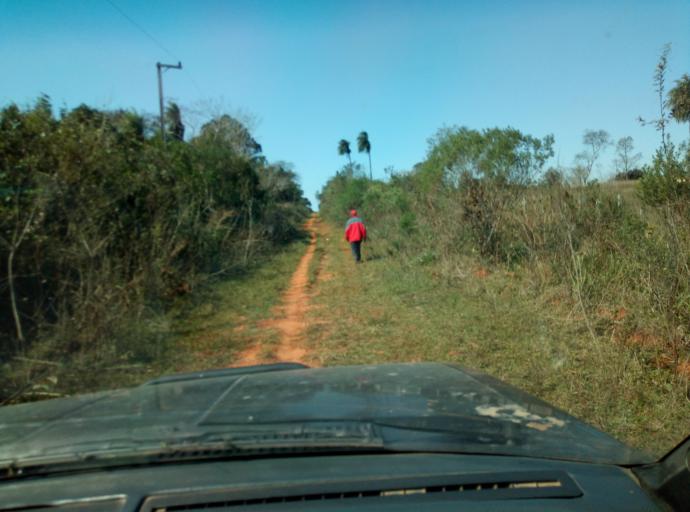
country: PY
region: Caaguazu
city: Doctor Cecilio Baez
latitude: -25.1793
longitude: -56.2151
